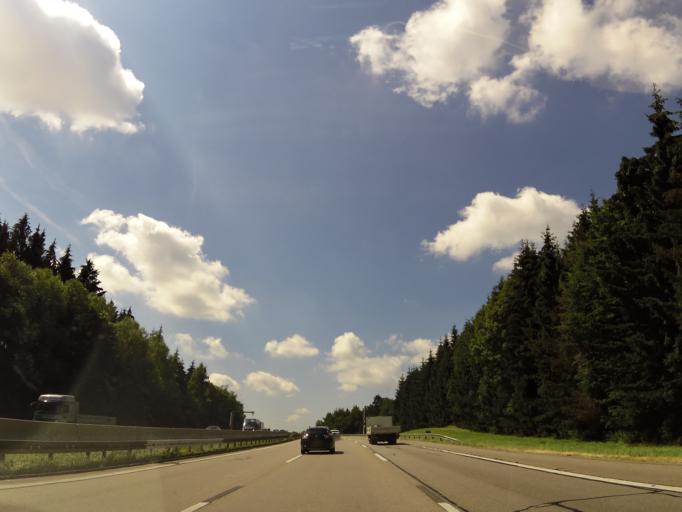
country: DE
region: Bavaria
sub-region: Upper Bavaria
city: Paunzhausen
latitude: 48.4806
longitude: 11.5870
